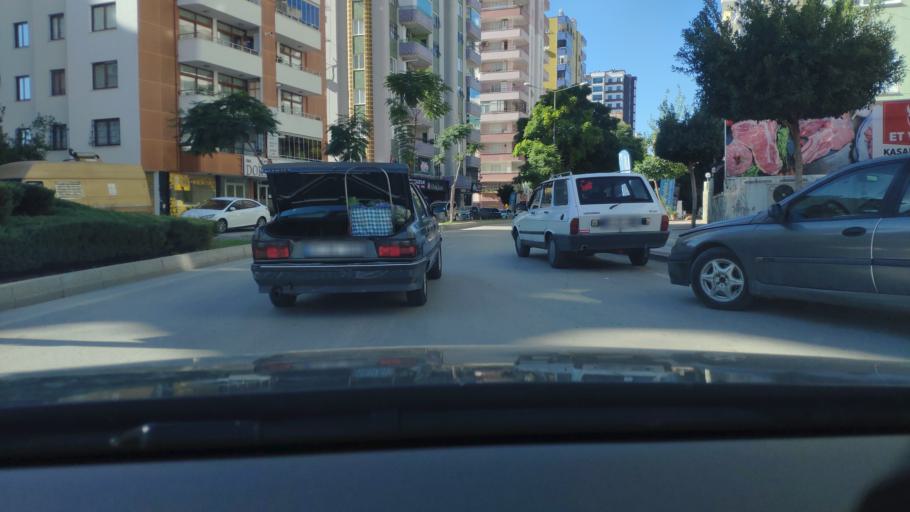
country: TR
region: Adana
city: Adana
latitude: 37.0531
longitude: 35.2823
